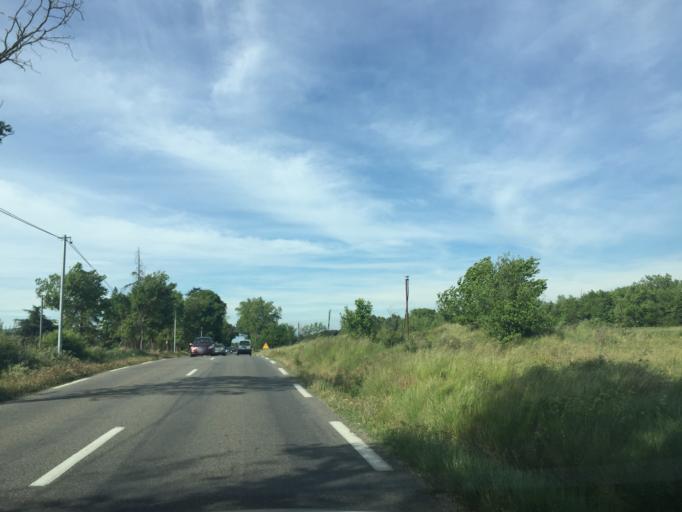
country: FR
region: Provence-Alpes-Cote d'Azur
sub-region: Departement du Var
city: Vinon-sur-Verdon
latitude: 43.7689
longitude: 5.8122
